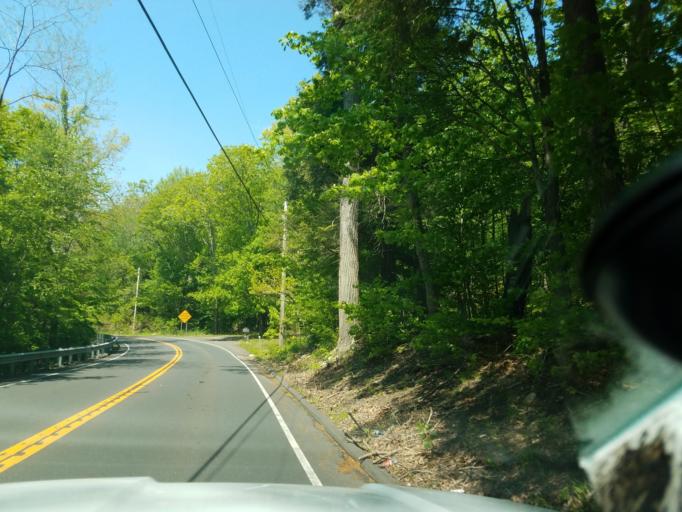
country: US
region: Connecticut
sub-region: New Haven County
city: Guilford
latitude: 41.3307
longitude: -72.7063
